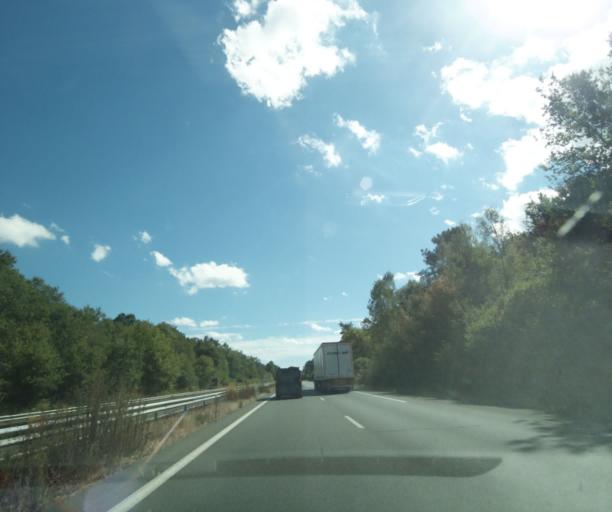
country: FR
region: Aquitaine
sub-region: Departement du Lot-et-Garonne
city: Fourques-sur-Garonne
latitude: 44.3954
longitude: 0.1931
